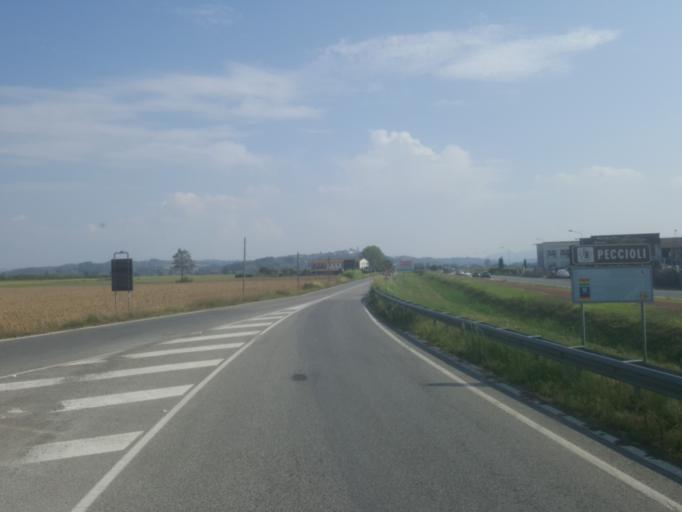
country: IT
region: Tuscany
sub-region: Province of Pisa
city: Selvatelle
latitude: 43.5800
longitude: 10.7045
